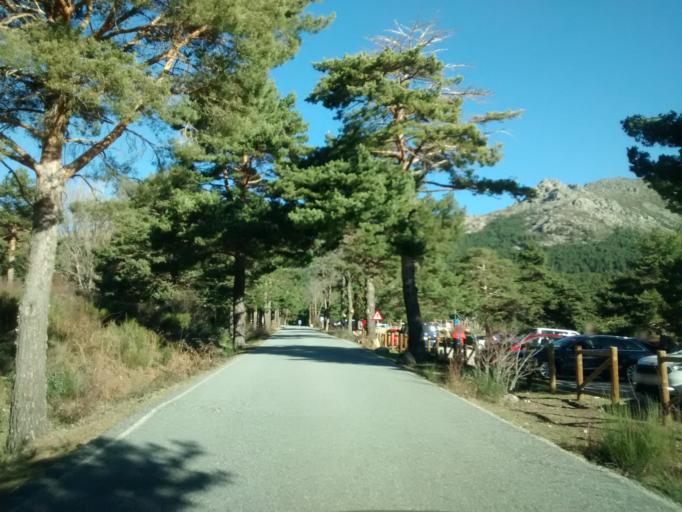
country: ES
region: Madrid
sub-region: Provincia de Madrid
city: Navacerrada
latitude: 40.7511
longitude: -3.9933
